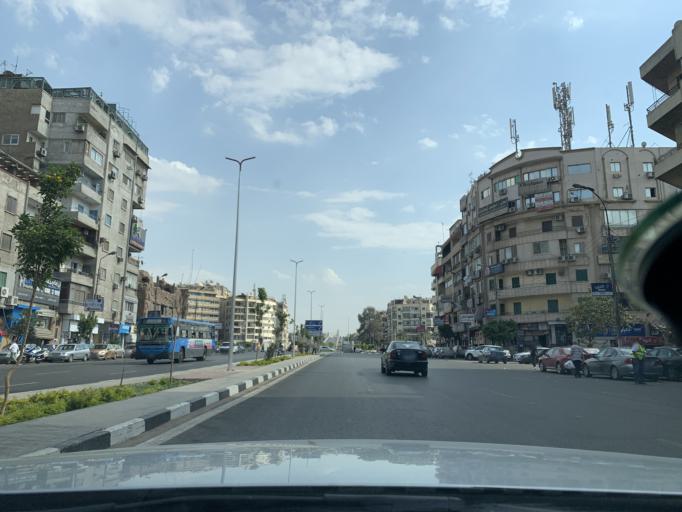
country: EG
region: Muhafazat al Qahirah
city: Cairo
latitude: 30.1021
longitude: 31.3433
